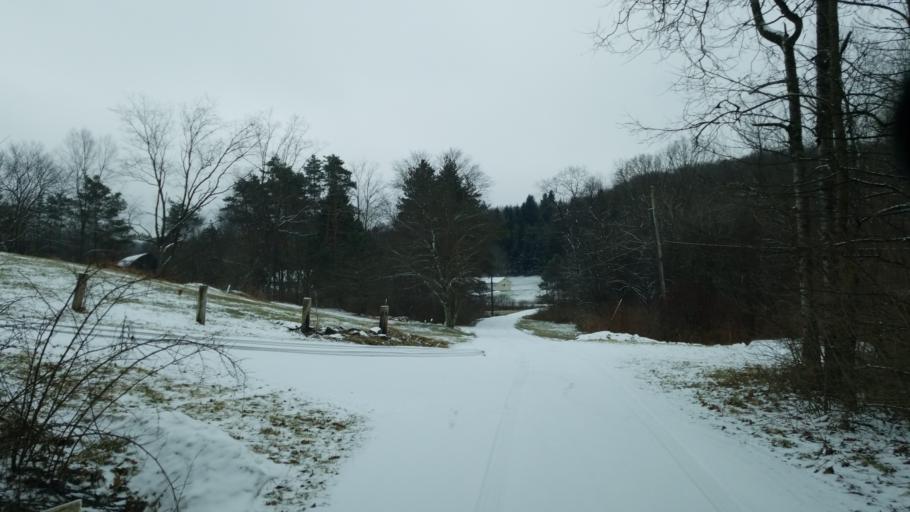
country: US
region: Pennsylvania
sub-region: Jefferson County
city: Sykesville
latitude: 41.0628
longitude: -78.8236
